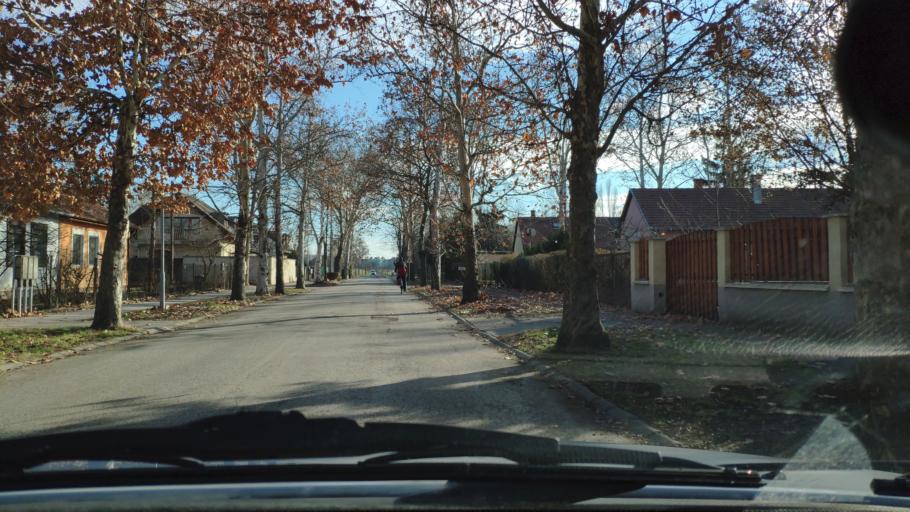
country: HU
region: Budapest
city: Budapest XXI. keruelet
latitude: 47.4098
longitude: 19.0661
